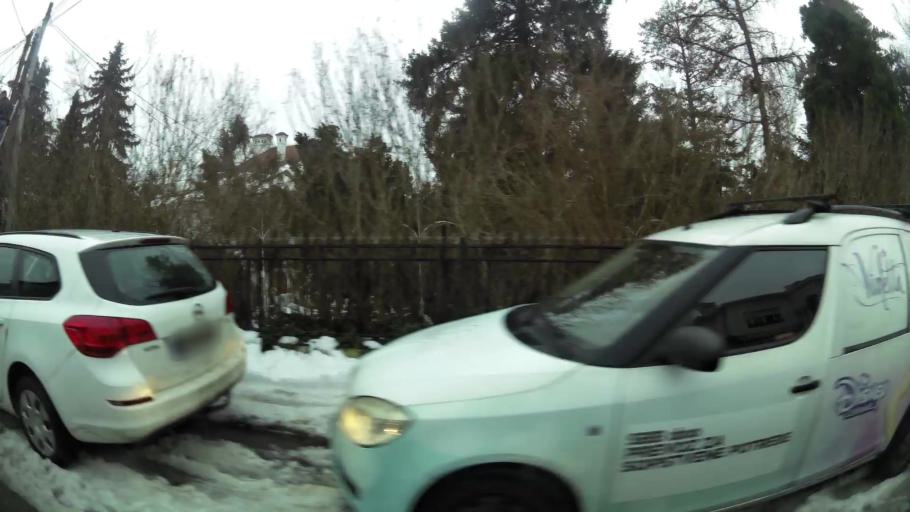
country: RS
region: Central Serbia
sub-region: Belgrade
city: Savski Venac
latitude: 44.7839
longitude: 20.4462
